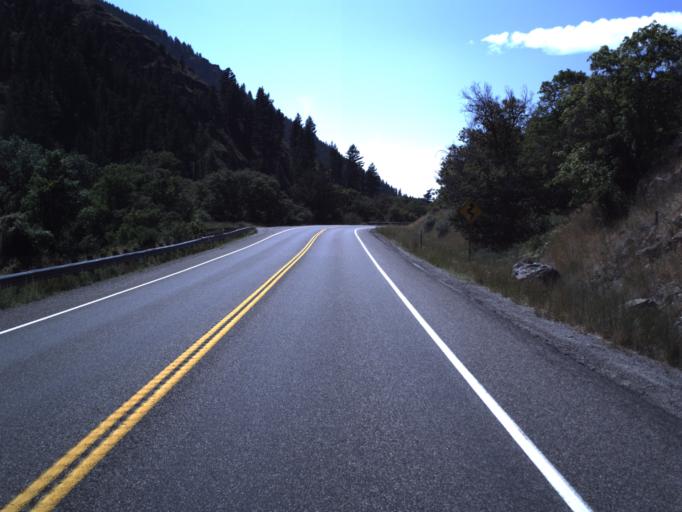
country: US
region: Utah
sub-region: Cache County
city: North Logan
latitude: 41.7652
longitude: -111.6871
